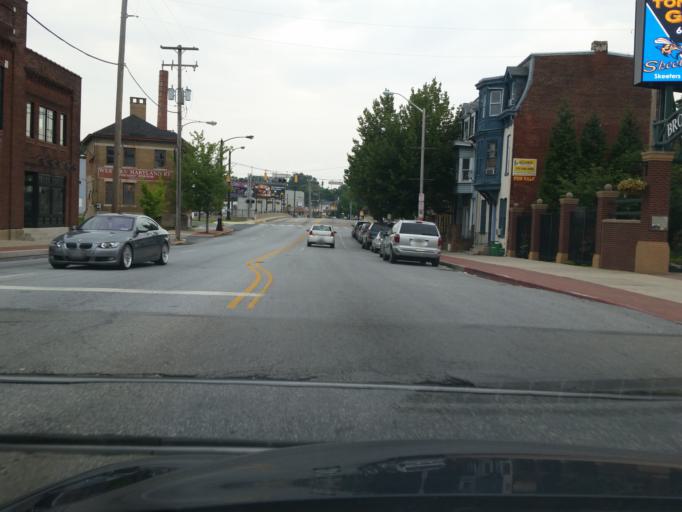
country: US
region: Pennsylvania
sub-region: York County
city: York
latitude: 39.9667
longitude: -76.7299
